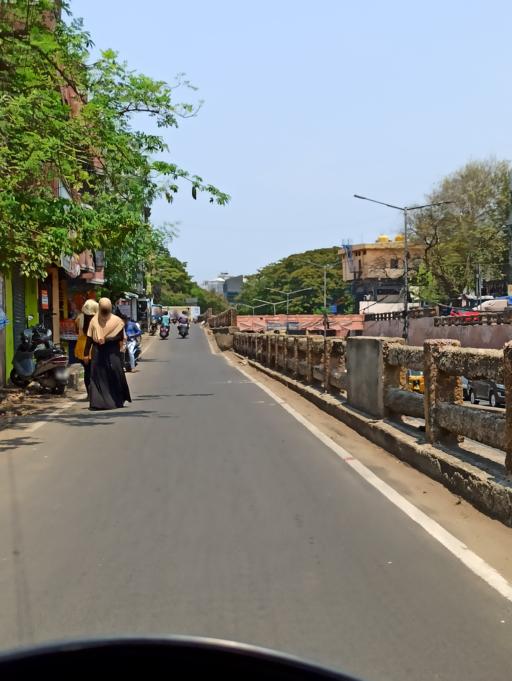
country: IN
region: Tamil Nadu
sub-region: Chennai
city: Chetput
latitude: 13.0665
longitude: 80.2317
